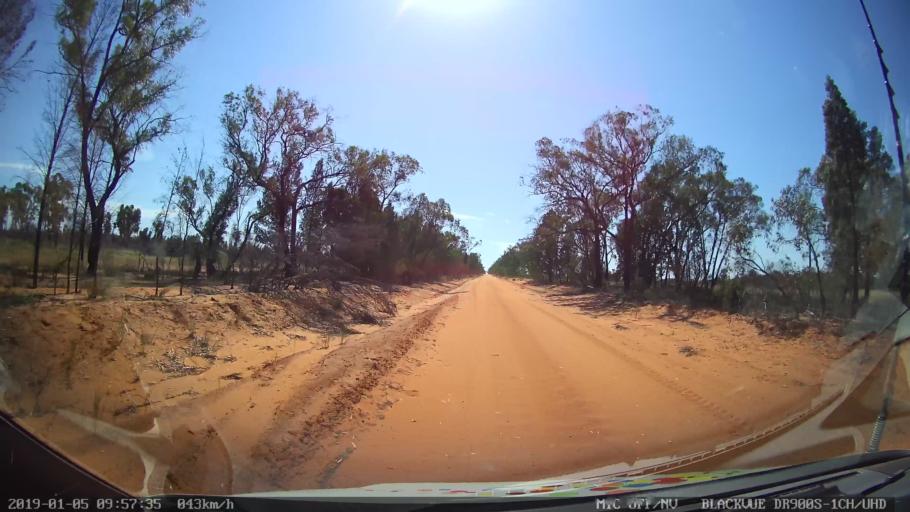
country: AU
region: New South Wales
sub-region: Gilgandra
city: Gilgandra
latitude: -31.6657
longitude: 148.8025
